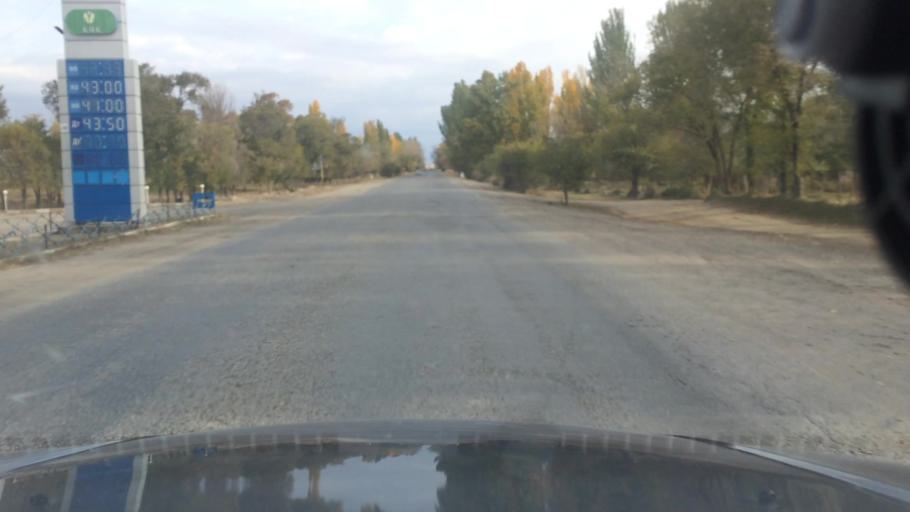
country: KG
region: Ysyk-Koel
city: Karakol
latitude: 42.5396
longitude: 78.3837
